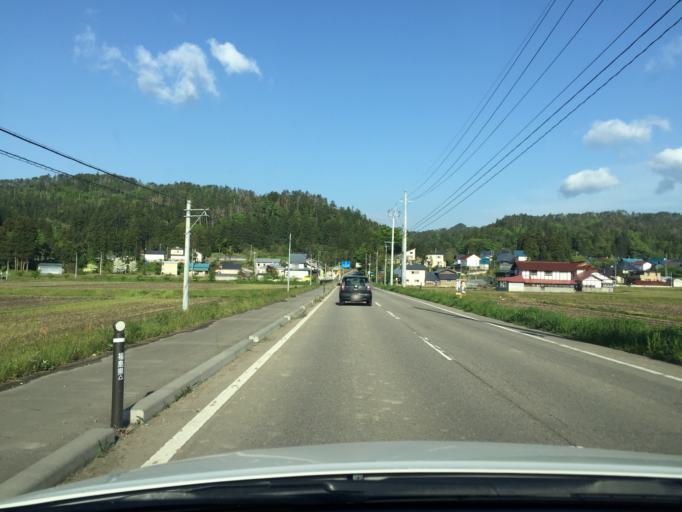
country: JP
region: Fukushima
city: Kitakata
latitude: 37.6663
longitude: 139.8495
